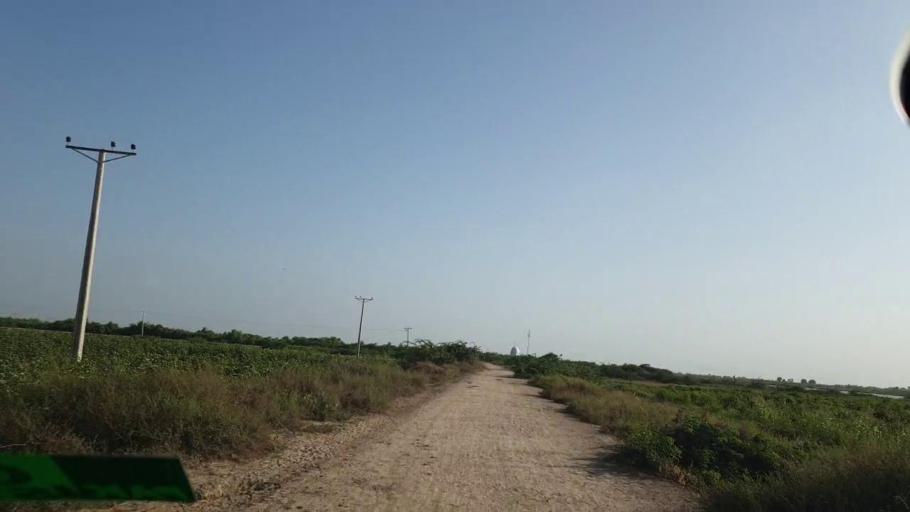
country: PK
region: Sindh
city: Naukot
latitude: 24.7385
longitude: 69.2477
